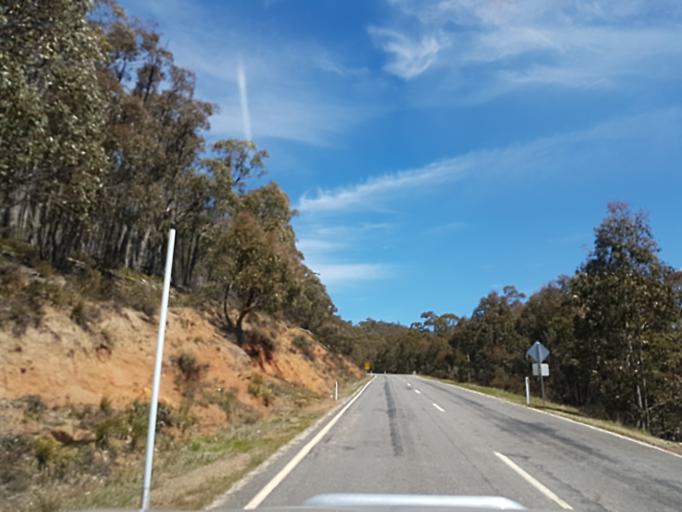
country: AU
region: Victoria
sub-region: Alpine
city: Mount Beauty
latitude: -37.0821
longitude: 147.3794
